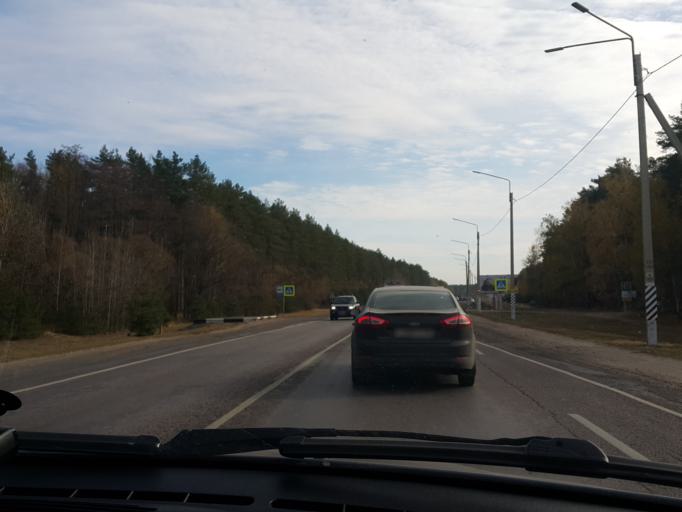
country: RU
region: Tambov
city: Donskoye
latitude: 52.7139
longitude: 41.5172
